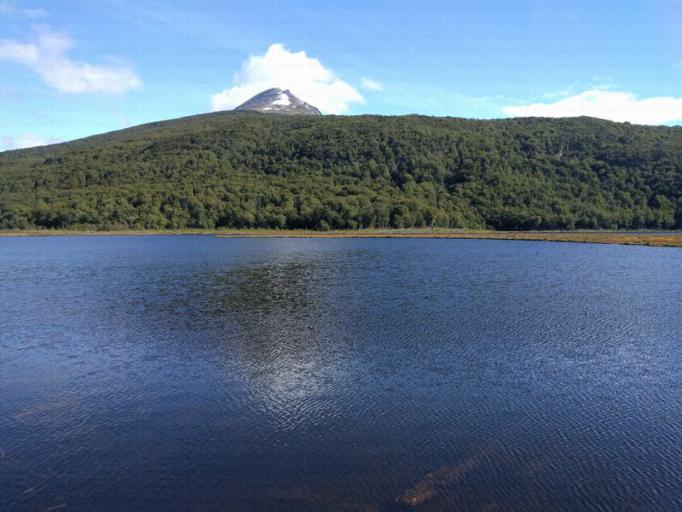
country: AR
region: Tierra del Fuego
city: Ushuaia
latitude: -54.8450
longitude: -68.5883
